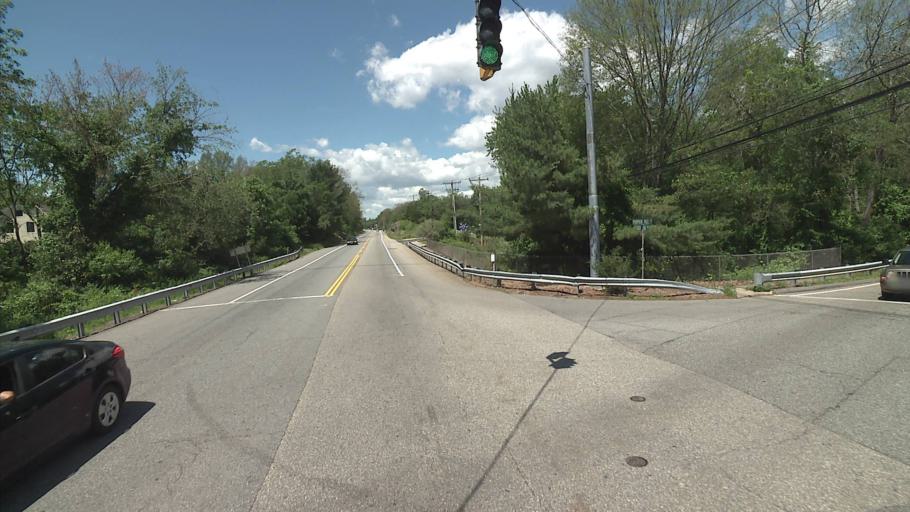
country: US
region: Connecticut
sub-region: New London County
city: Old Mystic
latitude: 41.3894
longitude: -71.9797
